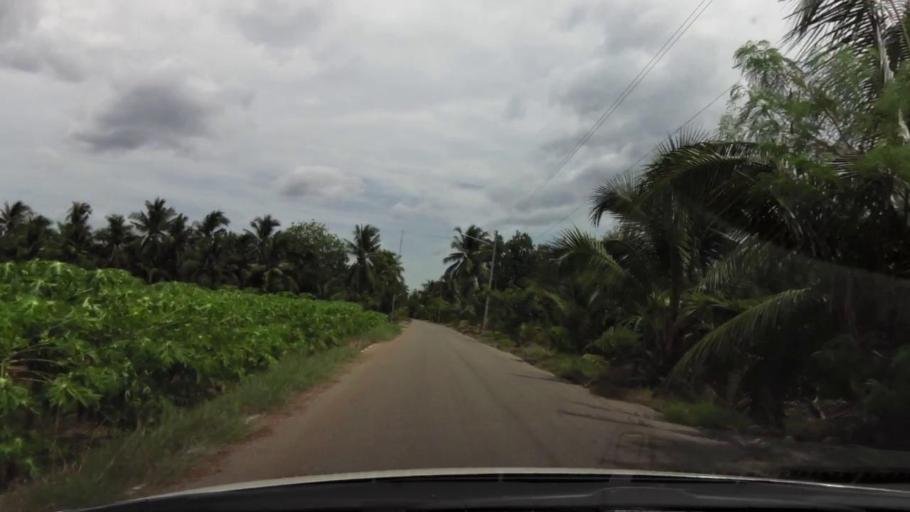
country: TH
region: Ratchaburi
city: Damnoen Saduak
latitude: 13.5328
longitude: 100.0008
